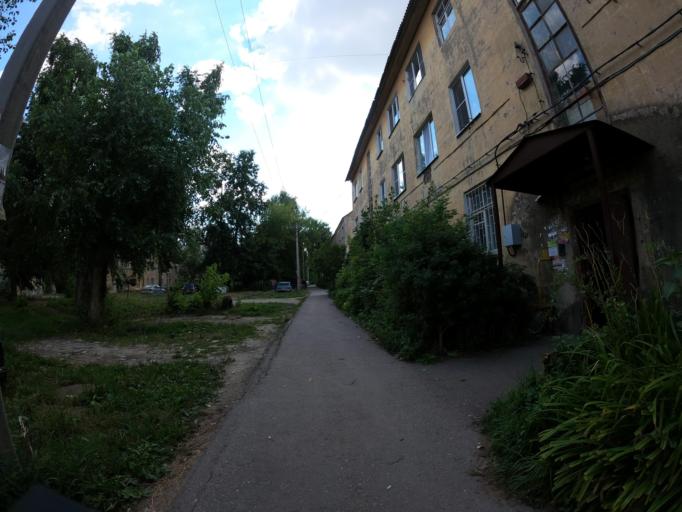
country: RU
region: Moskovskaya
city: Peski
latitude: 55.2706
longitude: 38.7353
